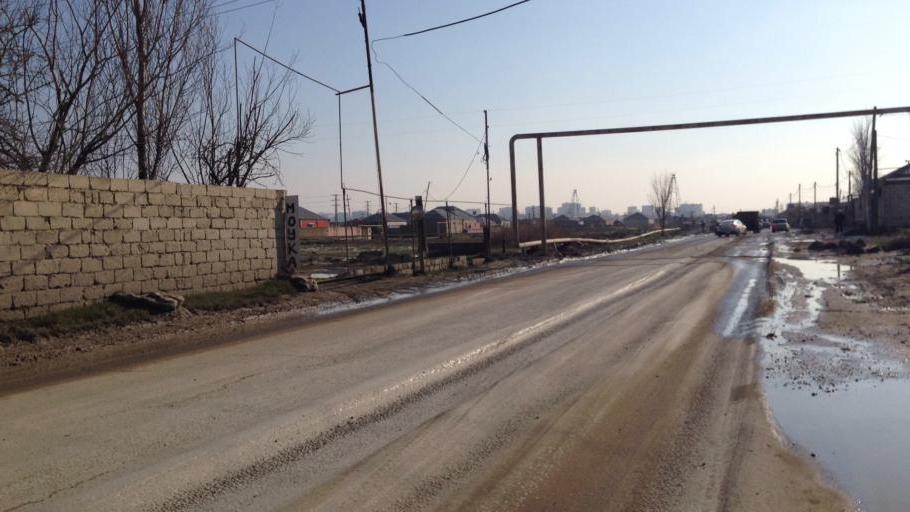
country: AZ
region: Baki
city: Balakhani
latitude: 40.4519
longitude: 49.9316
